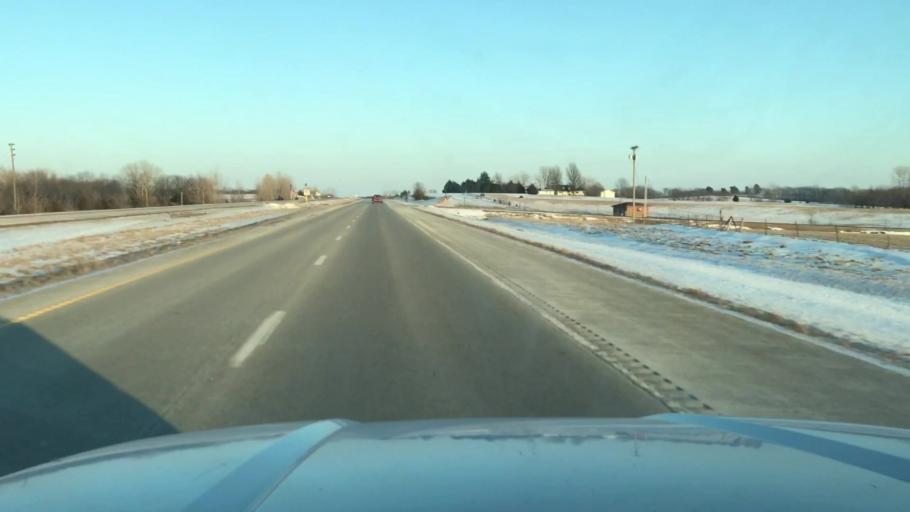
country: US
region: Missouri
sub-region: Clinton County
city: Gower
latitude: 39.7470
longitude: -94.6197
